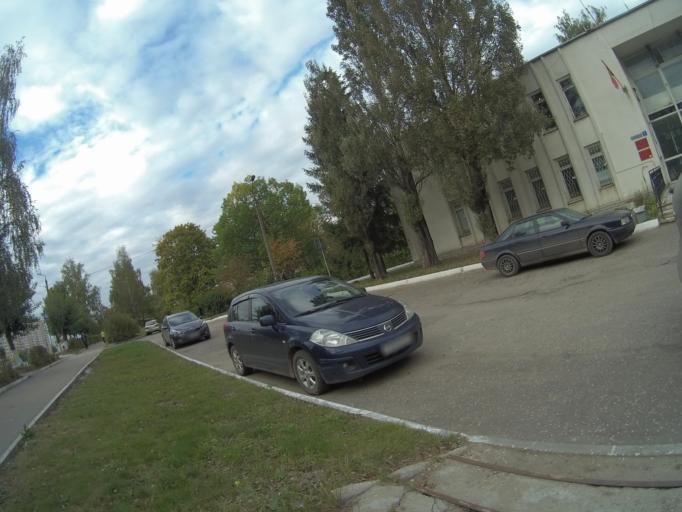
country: RU
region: Vladimir
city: Raduzhnyy
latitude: 56.1036
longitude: 40.2807
